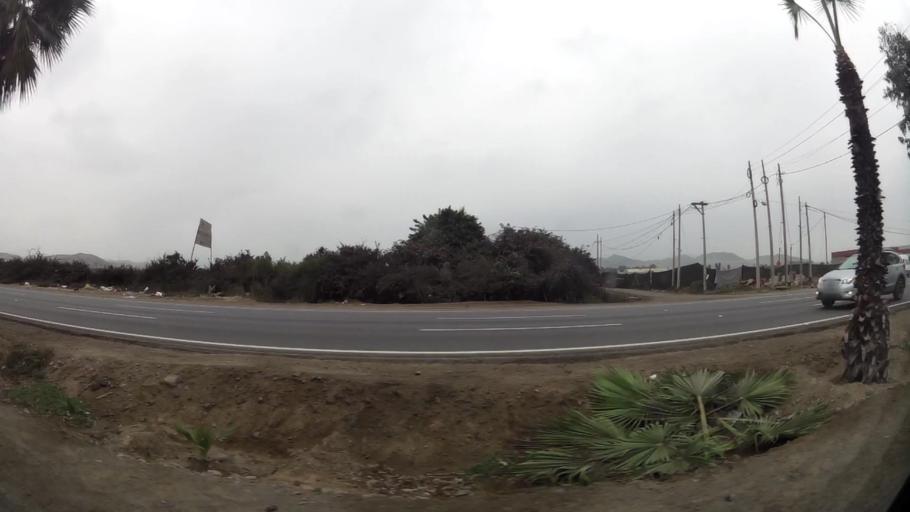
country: PE
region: Lima
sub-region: Lima
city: Punta Hermosa
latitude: -12.2742
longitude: -76.8928
